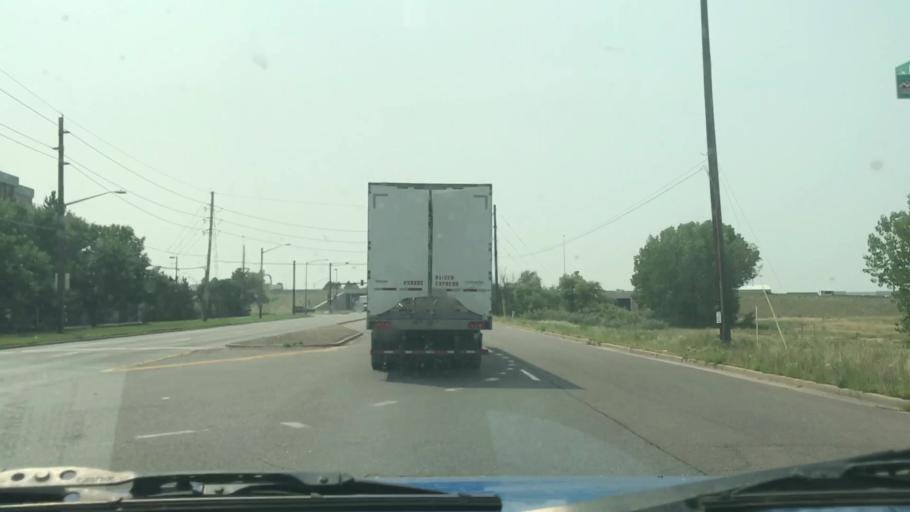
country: US
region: Colorado
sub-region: Adams County
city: Aurora
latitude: 39.7789
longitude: -104.8659
